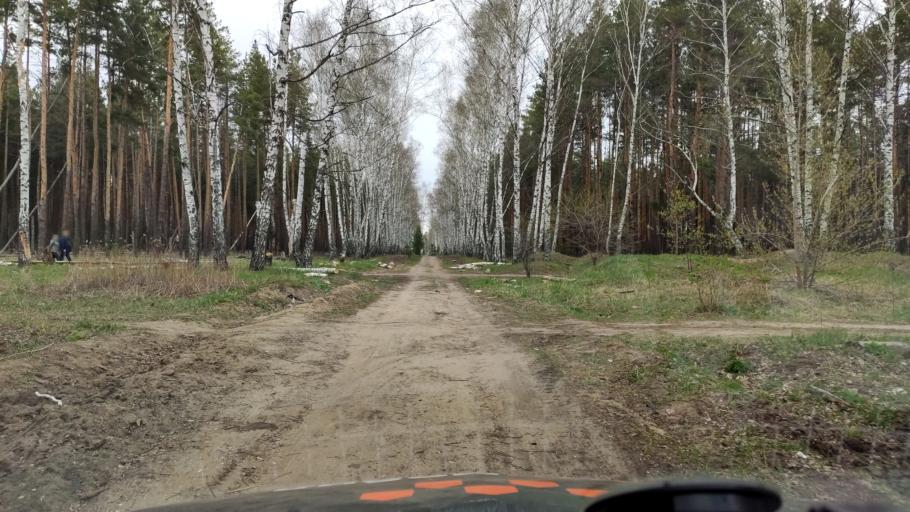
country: RU
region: Voronezj
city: Somovo
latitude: 51.7444
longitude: 39.2752
